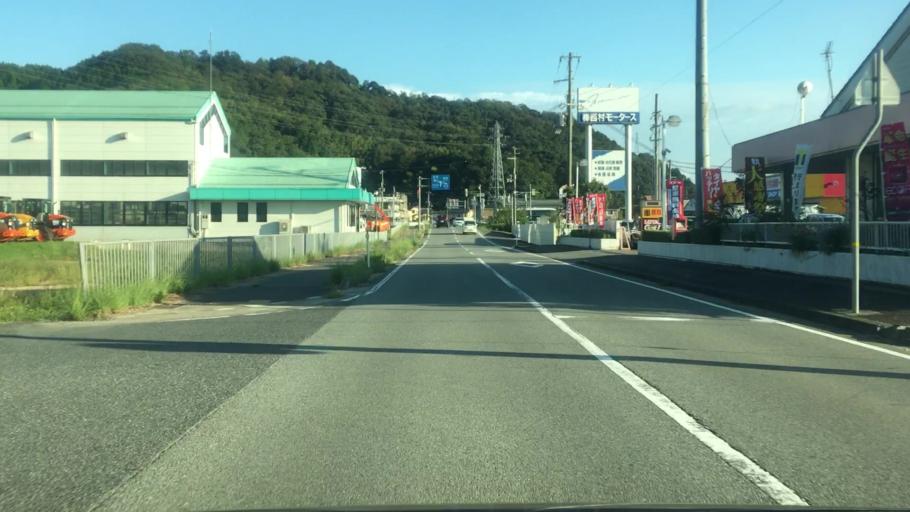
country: JP
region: Hyogo
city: Toyooka
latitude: 35.5601
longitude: 134.8237
